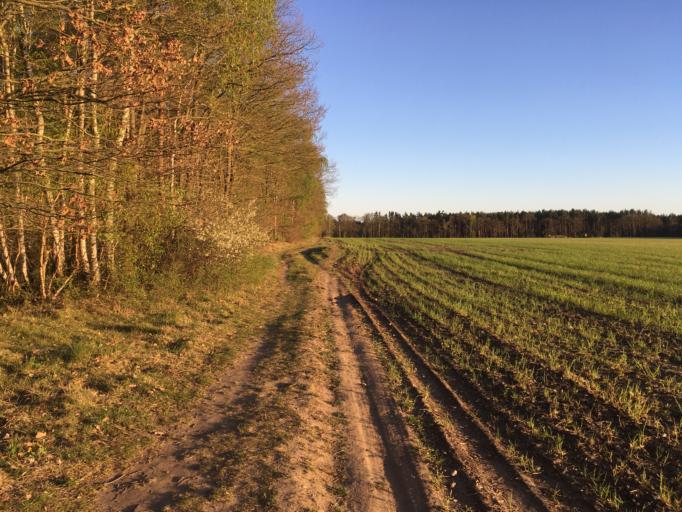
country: DE
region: Lower Saxony
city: Wendisch Evern
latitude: 53.2261
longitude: 10.4426
